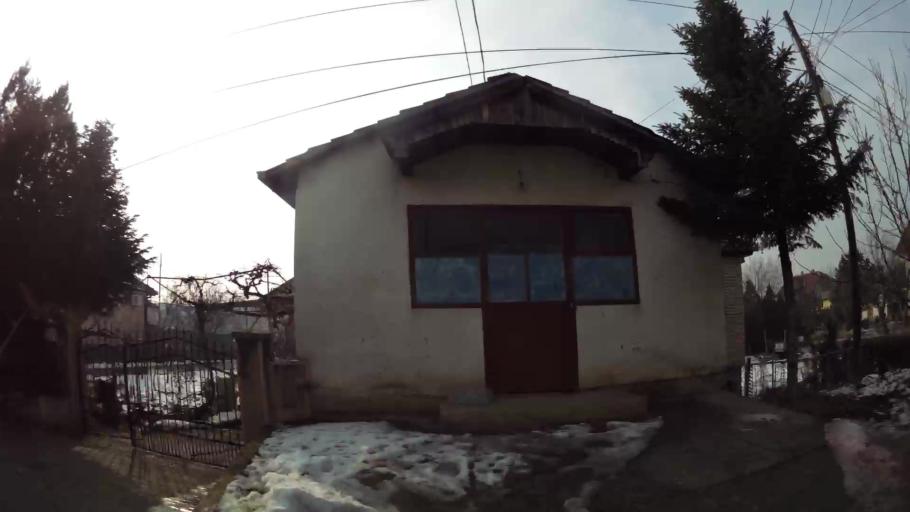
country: MK
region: Ilinden
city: Marino
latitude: 41.9911
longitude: 21.5903
